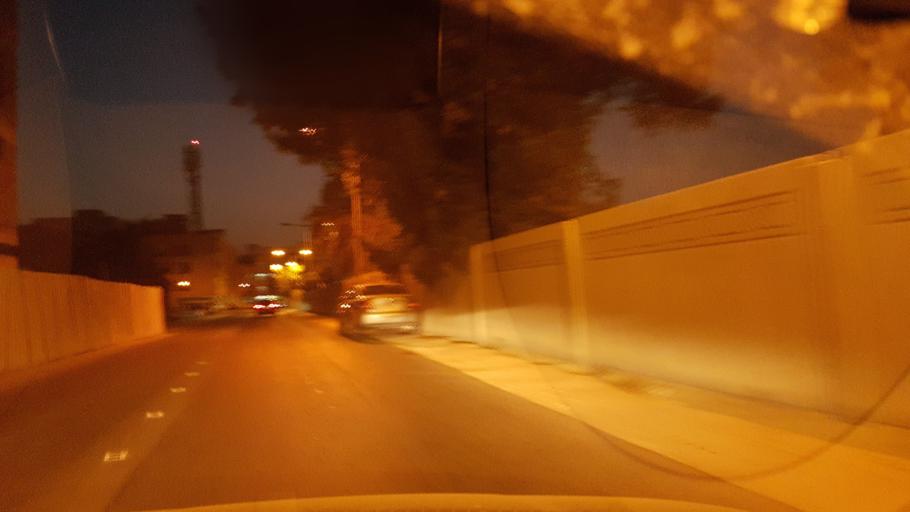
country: BH
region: Manama
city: Manama
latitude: 26.2220
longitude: 50.5819
